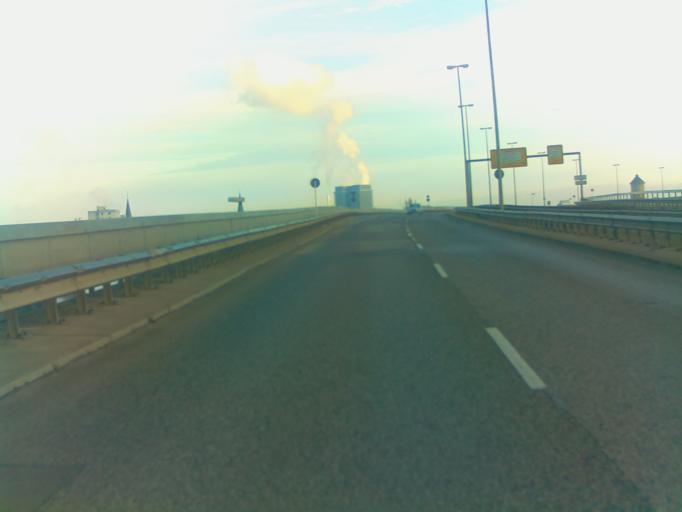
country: DE
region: Rheinland-Pfalz
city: Ludwigshafen am Rhein
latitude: 49.4793
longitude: 8.4304
